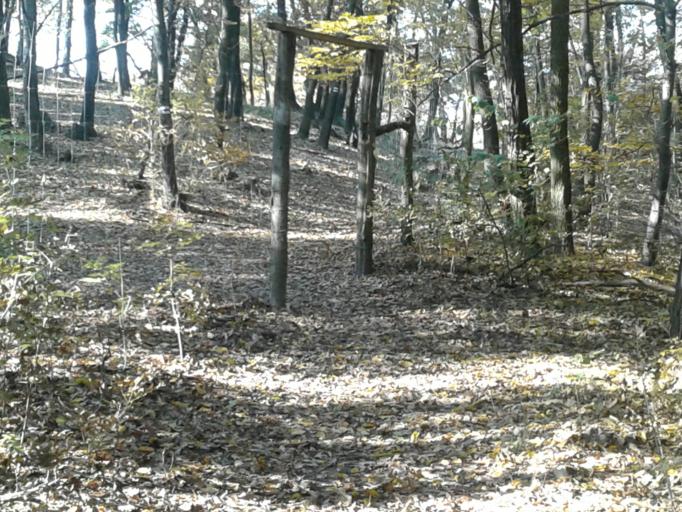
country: HU
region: Fejer
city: Bodajk
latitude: 47.3146
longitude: 18.2180
